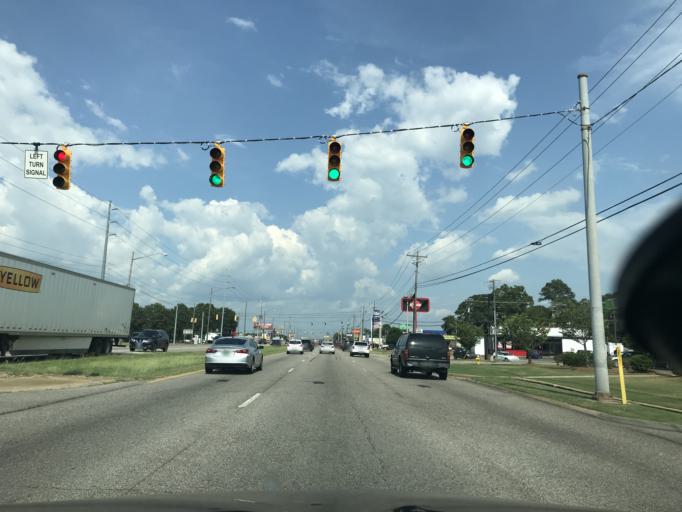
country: US
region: Alabama
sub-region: Montgomery County
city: Montgomery
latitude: 32.3819
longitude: -86.2068
